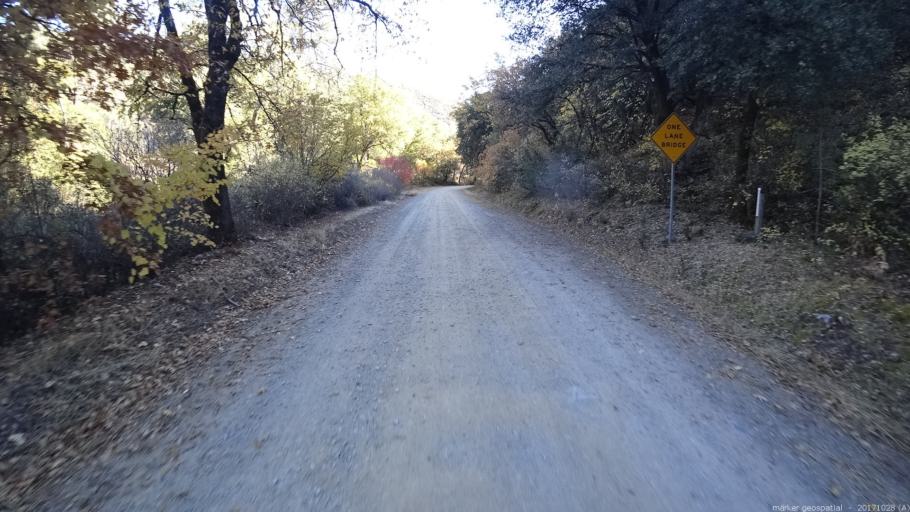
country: US
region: California
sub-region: Trinity County
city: Lewiston
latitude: 40.7152
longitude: -122.6300
